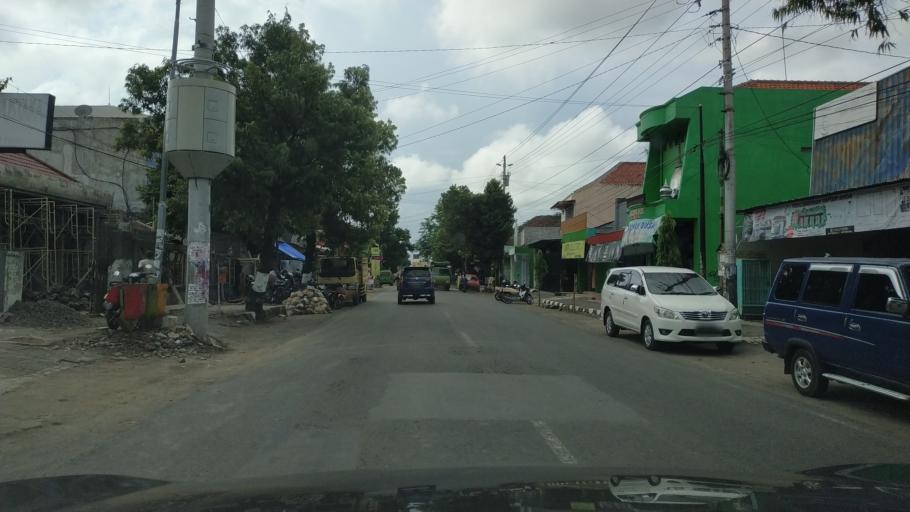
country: ID
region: Central Java
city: Pemalang
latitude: -6.8921
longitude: 109.3826
